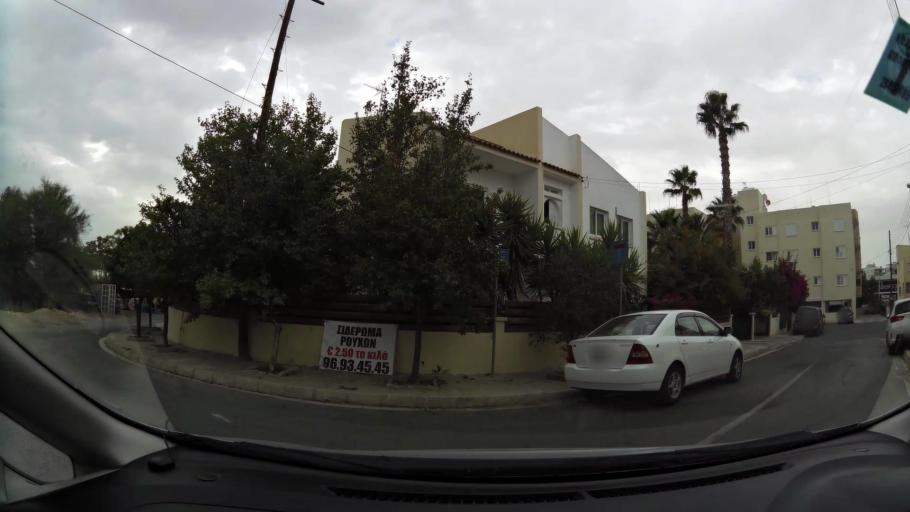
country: CY
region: Lefkosia
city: Geri
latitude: 35.1152
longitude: 33.3784
